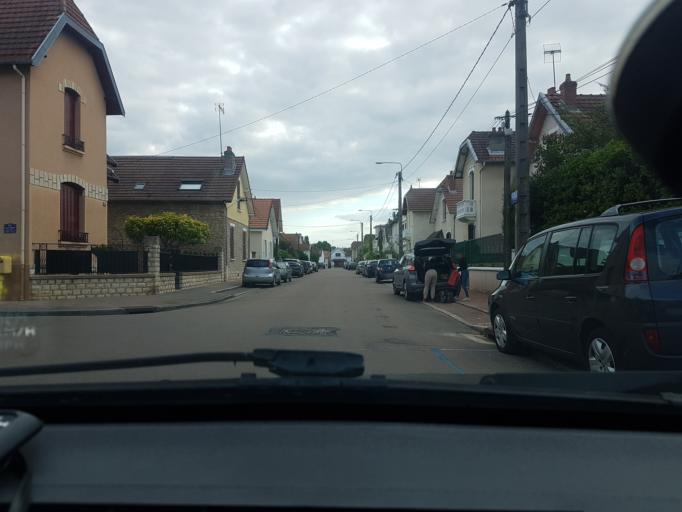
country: FR
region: Bourgogne
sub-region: Departement de la Cote-d'Or
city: Longvic
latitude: 47.3058
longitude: 5.0450
